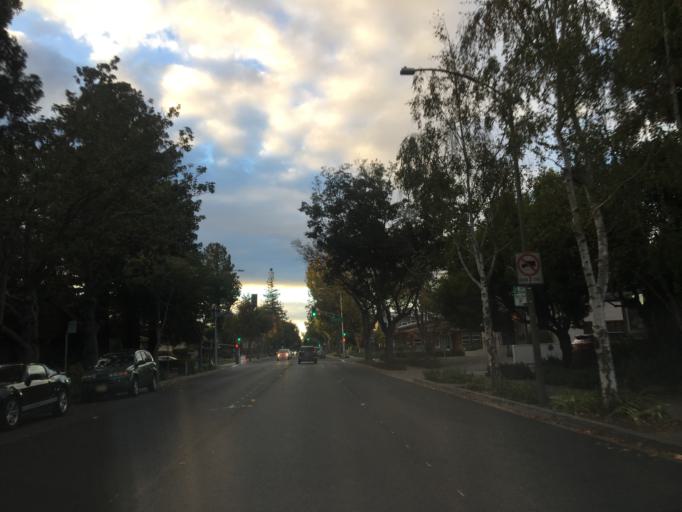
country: US
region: California
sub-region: Santa Clara County
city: Palo Alto
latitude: 37.4472
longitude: -122.1511
